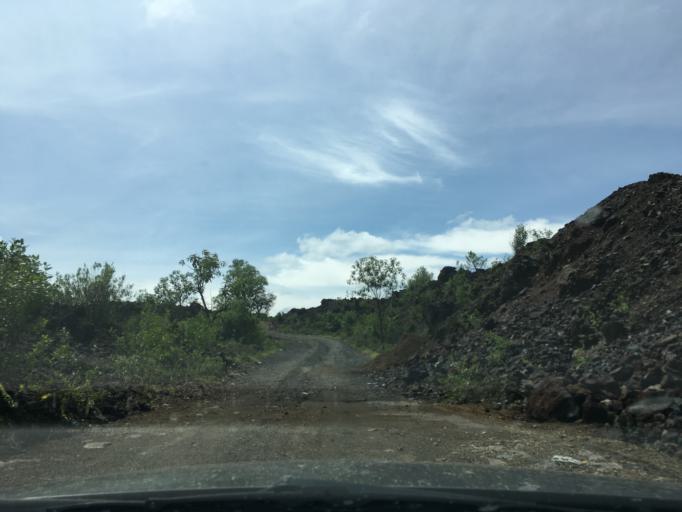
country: MX
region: Michoacan
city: Angahuan
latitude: 19.5242
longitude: -102.2301
